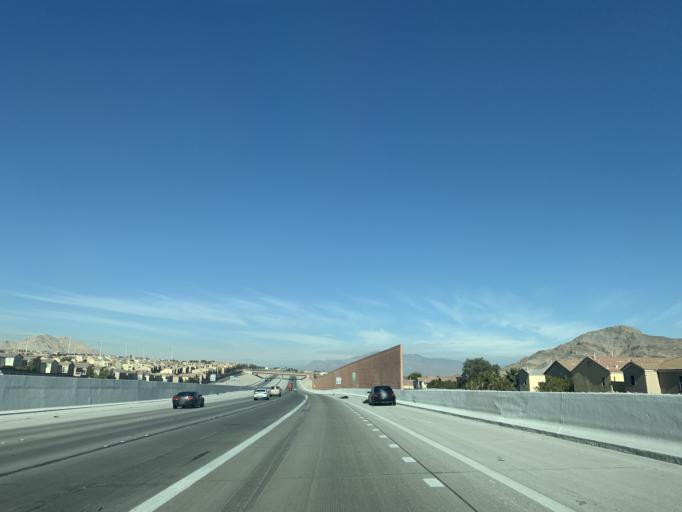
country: US
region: Nevada
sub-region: Clark County
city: Summerlin South
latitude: 36.2251
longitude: -115.3253
